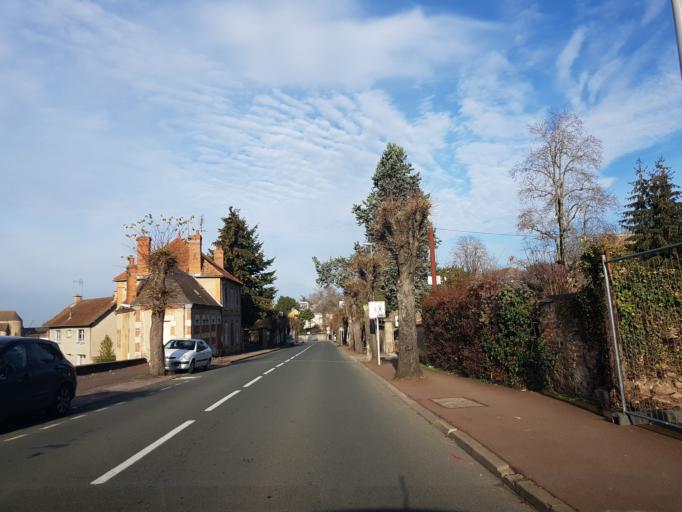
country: FR
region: Bourgogne
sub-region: Departement de Saone-et-Loire
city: Bourbon-Lancy
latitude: 46.6213
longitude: 3.7712
